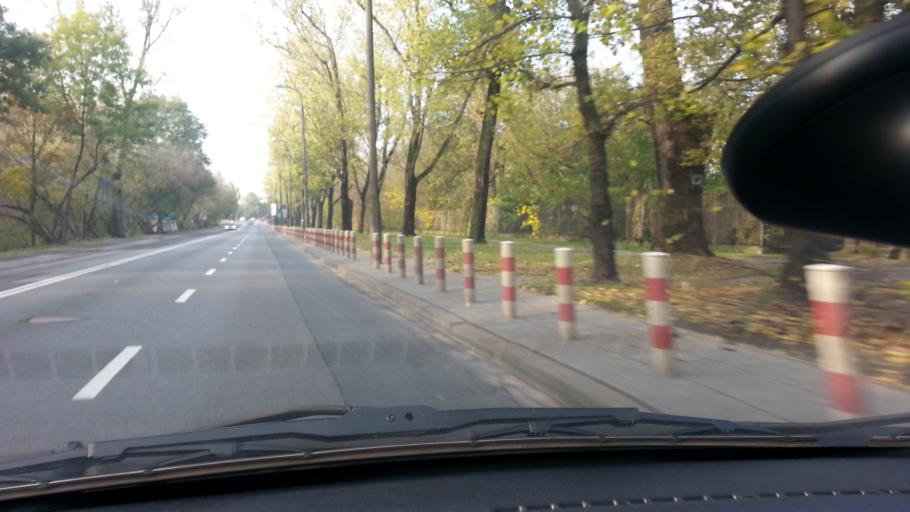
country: PL
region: Masovian Voivodeship
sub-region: Warszawa
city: Praga Polnoc
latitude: 52.2587
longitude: 21.0177
